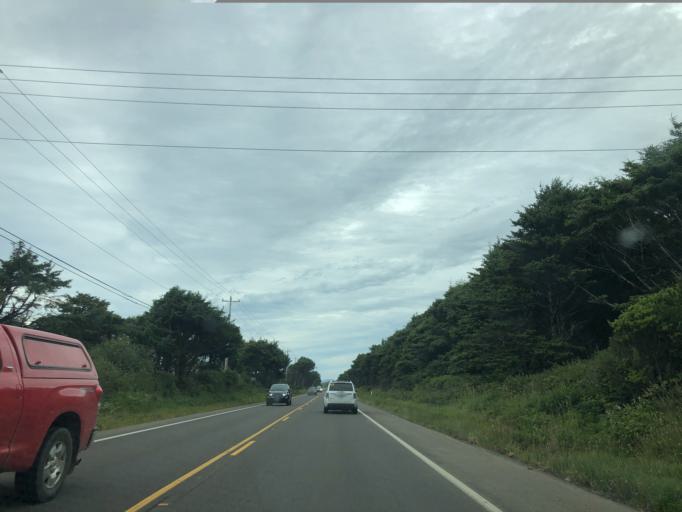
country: US
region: Oregon
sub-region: Lincoln County
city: Newport
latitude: 44.5356
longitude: -124.0744
